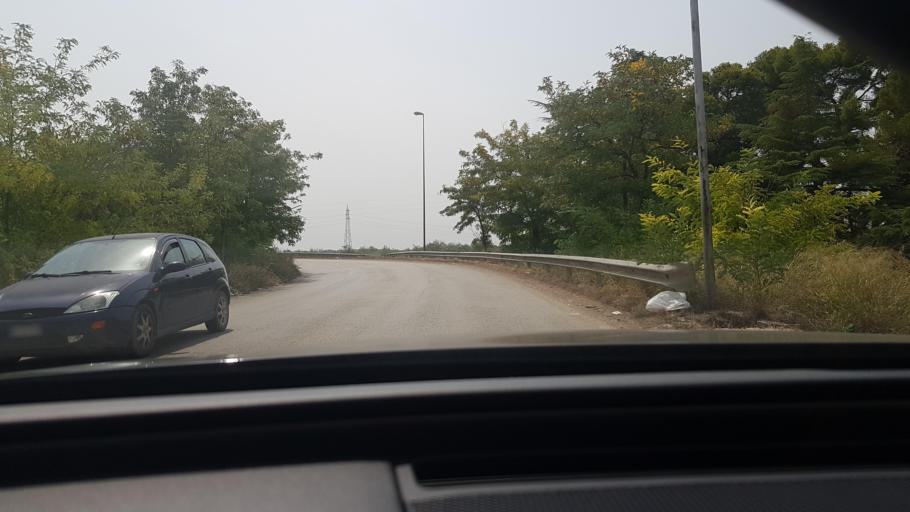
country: IT
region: Apulia
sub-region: Provincia di Barletta - Andria - Trani
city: Andria
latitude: 41.2150
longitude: 16.2650
